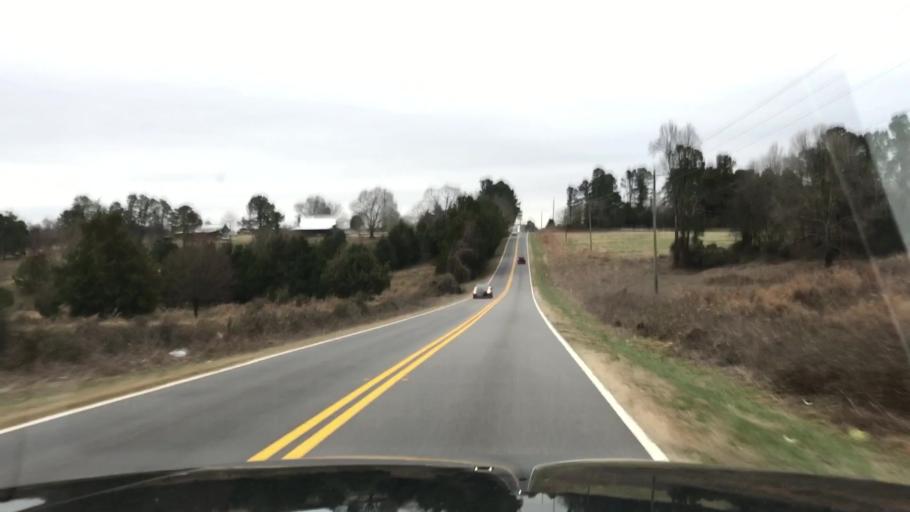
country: US
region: Georgia
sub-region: Barrow County
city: Auburn
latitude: 33.9099
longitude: -83.8161
